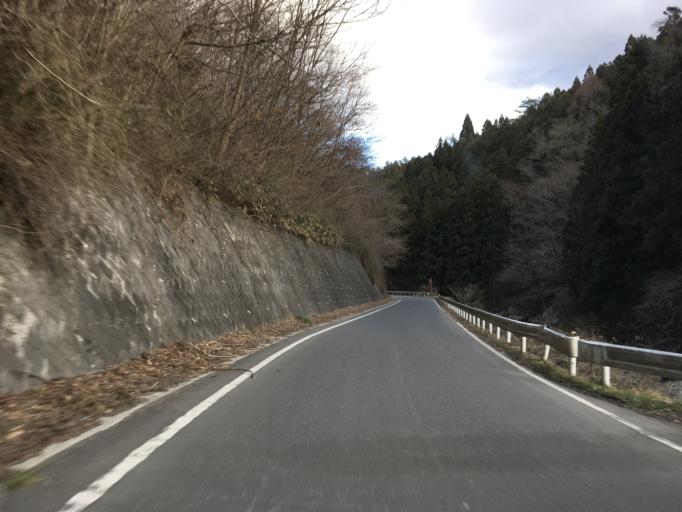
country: JP
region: Miyagi
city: Wakuya
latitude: 38.7188
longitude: 141.3101
